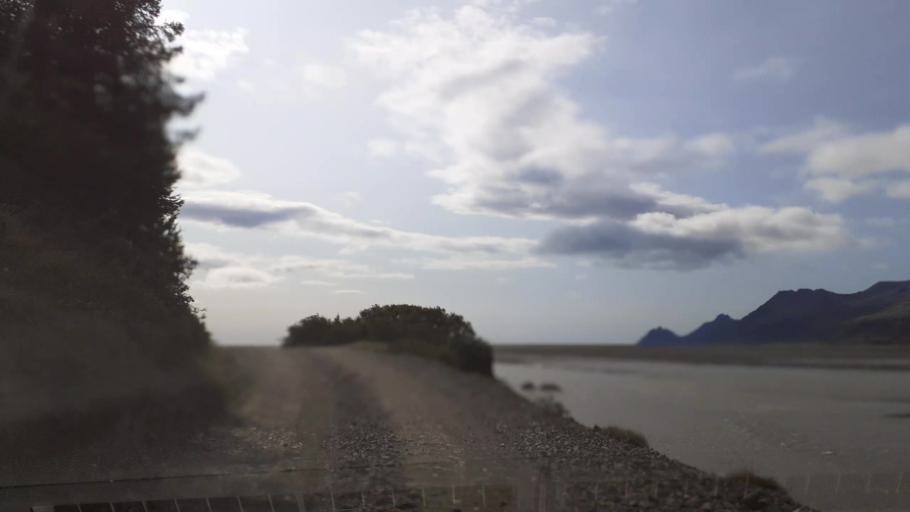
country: IS
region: East
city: Hoefn
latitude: 64.4364
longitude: -14.9080
